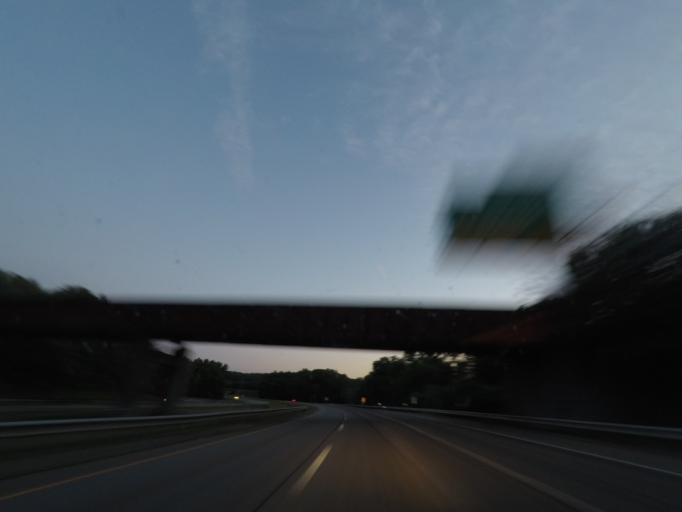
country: US
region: Connecticut
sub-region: Windham County
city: Putnam
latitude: 41.9040
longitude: -71.8968
